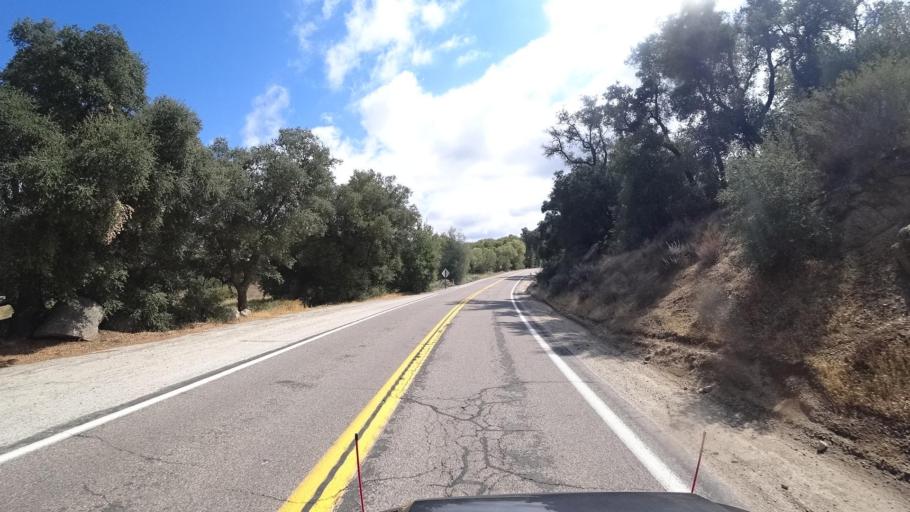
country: US
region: California
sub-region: San Diego County
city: Campo
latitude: 32.7123
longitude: -116.4942
